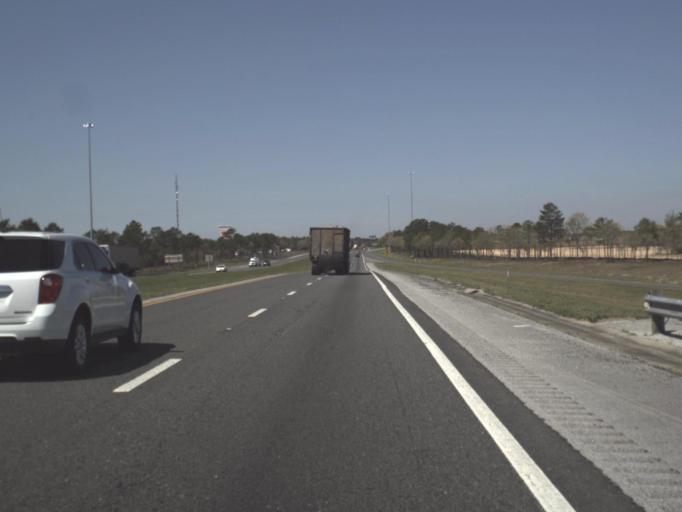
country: US
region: Florida
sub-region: Okaloosa County
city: Crestview
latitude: 30.7328
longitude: -86.3522
